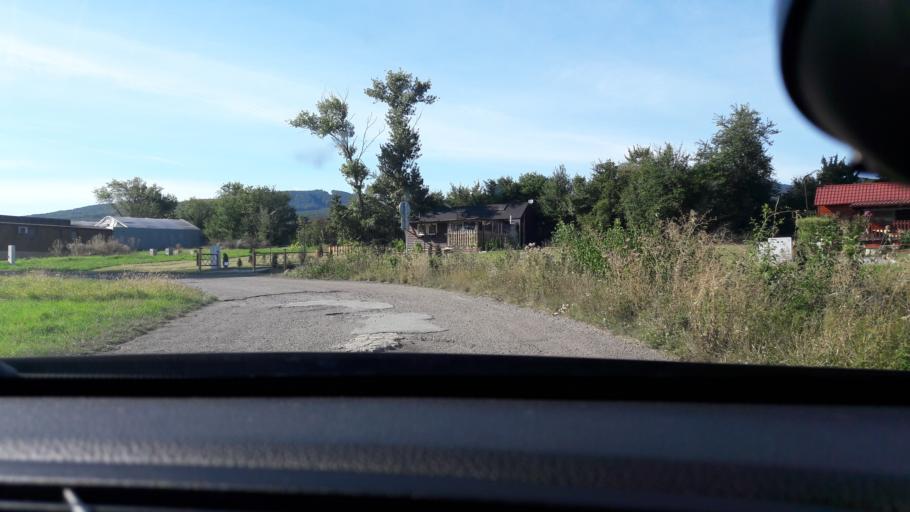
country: SK
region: Kosicky
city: Vinne
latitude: 48.8102
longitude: 22.0391
